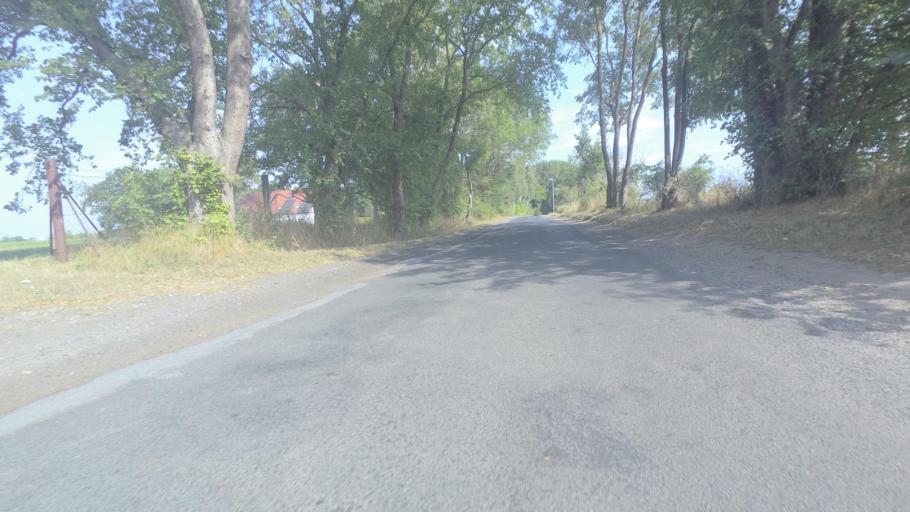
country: DE
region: Mecklenburg-Vorpommern
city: Wendorf
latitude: 54.2689
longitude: 13.0895
